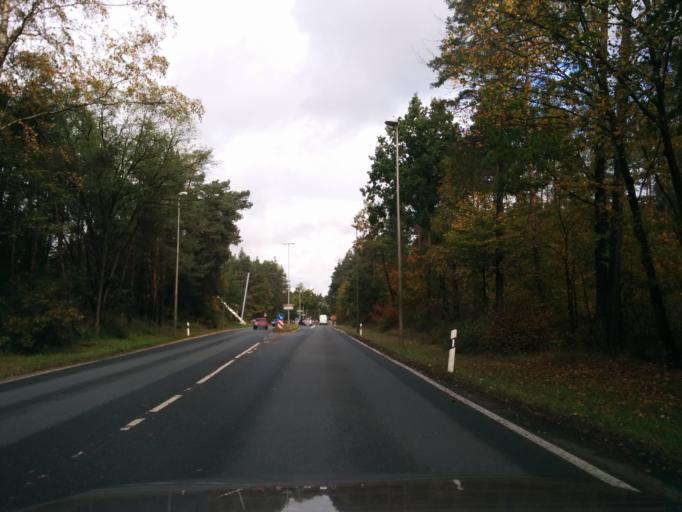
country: DE
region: Bavaria
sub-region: Regierungsbezirk Mittelfranken
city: Buckenhof
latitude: 49.5715
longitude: 11.0316
